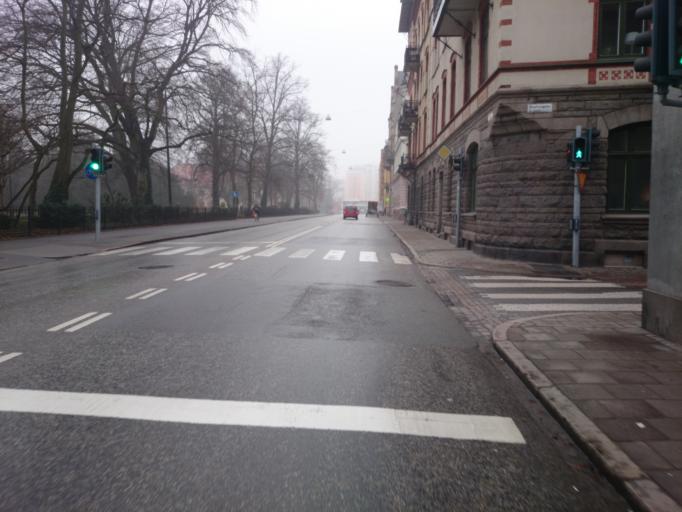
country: SE
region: Skane
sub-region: Malmo
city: Malmoe
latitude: 55.6041
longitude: 12.9938
